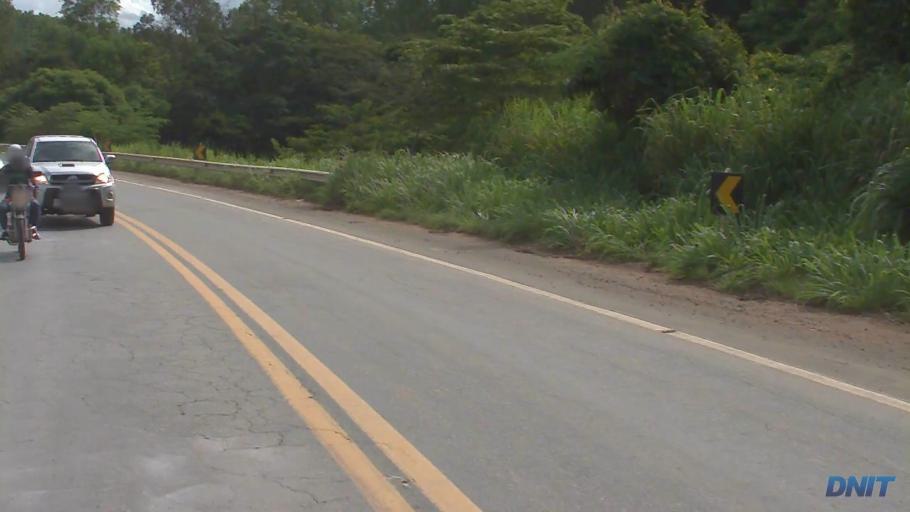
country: BR
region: Minas Gerais
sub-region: Ipaba
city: Ipaba
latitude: -19.3354
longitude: -42.4247
